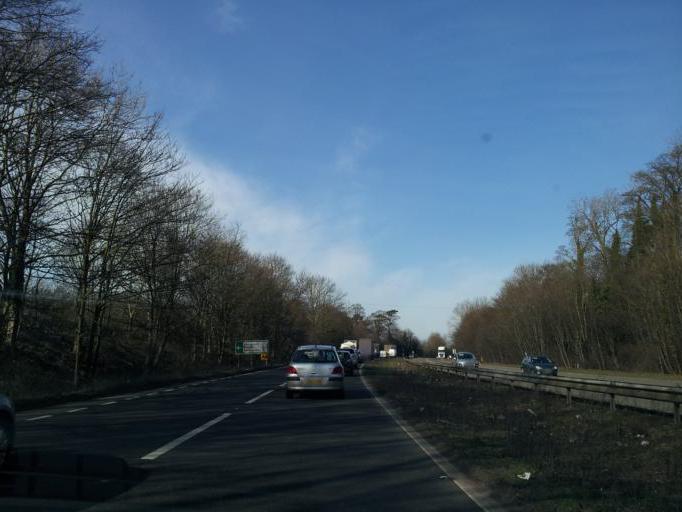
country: GB
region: England
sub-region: Lincolnshire
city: Grantham
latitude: 52.8266
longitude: -0.6304
